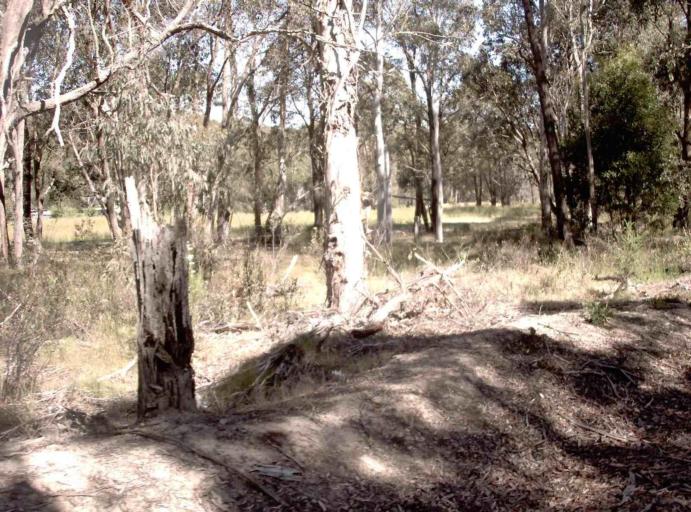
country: AU
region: New South Wales
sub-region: Bombala
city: Bombala
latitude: -37.1427
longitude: 148.7233
